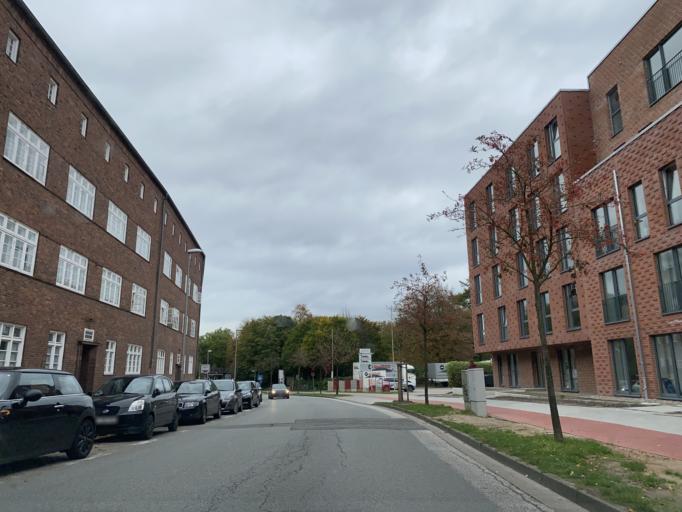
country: DE
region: Schleswig-Holstein
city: Flensburg
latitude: 54.7785
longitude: 9.4385
